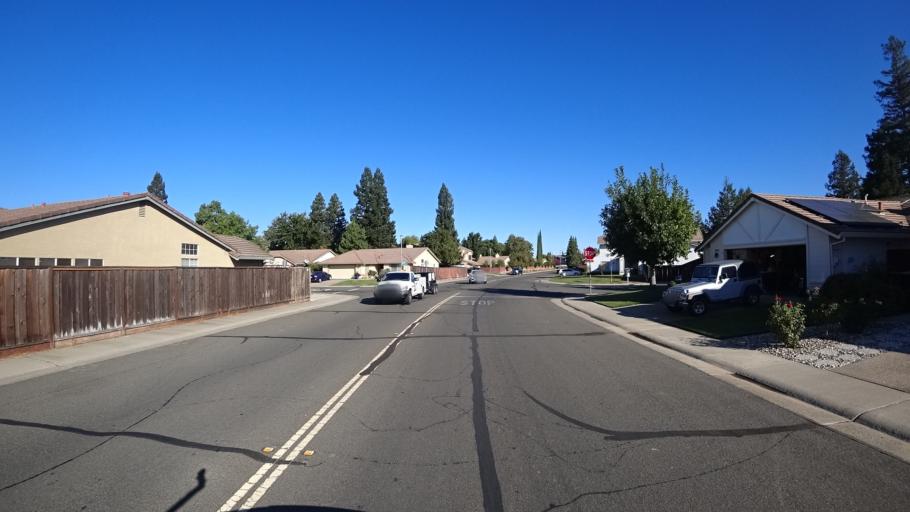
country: US
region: California
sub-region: Sacramento County
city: Elk Grove
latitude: 38.4361
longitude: -121.3795
